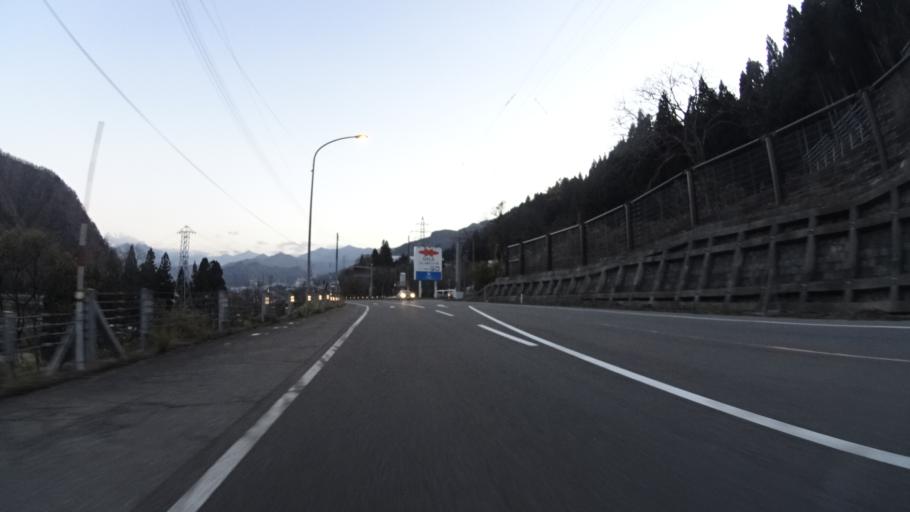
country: JP
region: Niigata
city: Shiozawa
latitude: 36.9556
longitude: 138.7991
